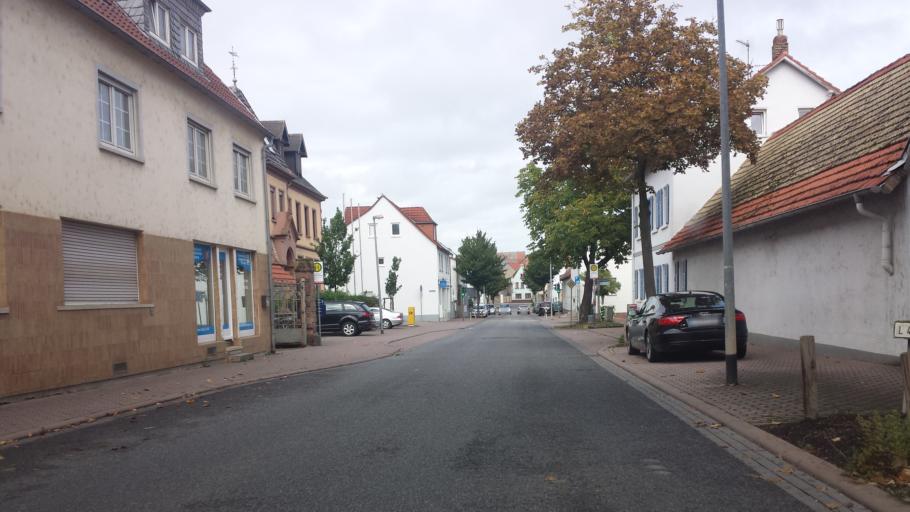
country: DE
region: Rheinland-Pfalz
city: Westhofen
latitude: 49.7016
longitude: 8.2486
